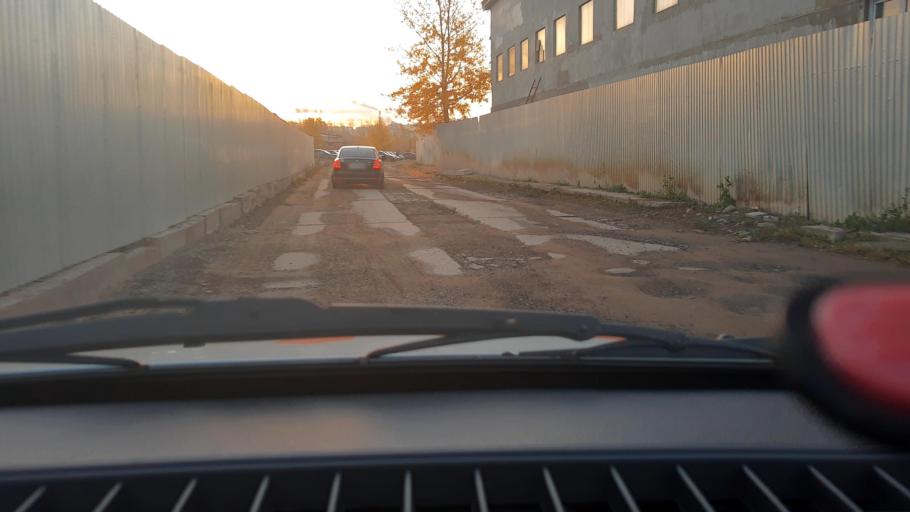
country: RU
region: Bashkortostan
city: Ufa
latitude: 54.7518
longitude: 55.9119
